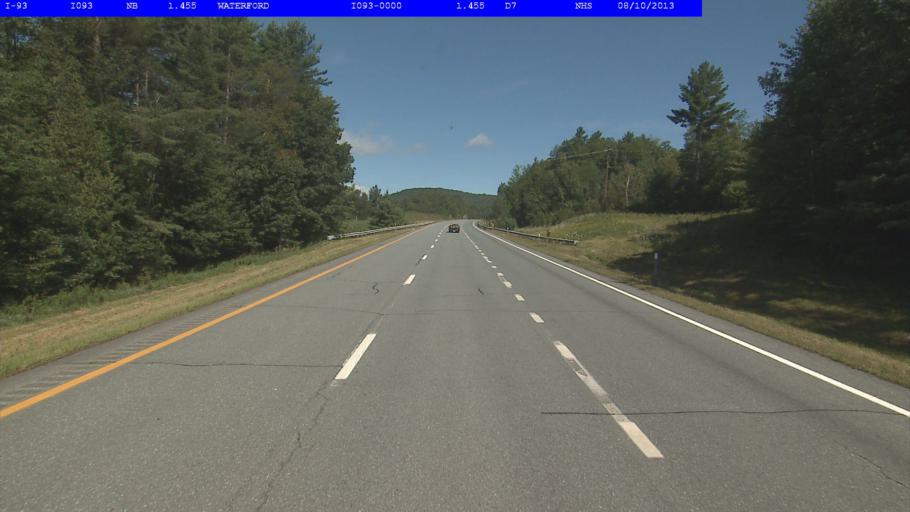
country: US
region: Vermont
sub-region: Caledonia County
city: Saint Johnsbury
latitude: 44.3631
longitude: -71.8999
